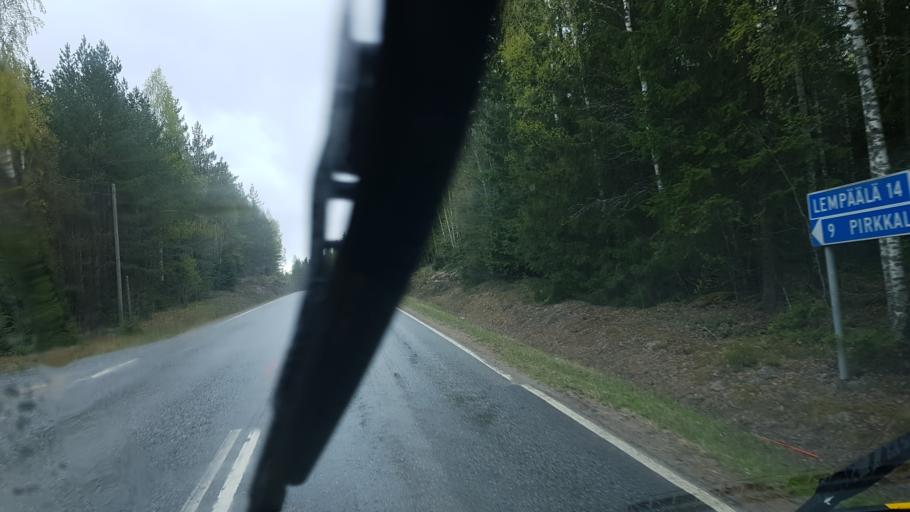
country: FI
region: Pirkanmaa
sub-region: Tampere
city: Pirkkala
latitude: 61.3954
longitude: 23.6257
